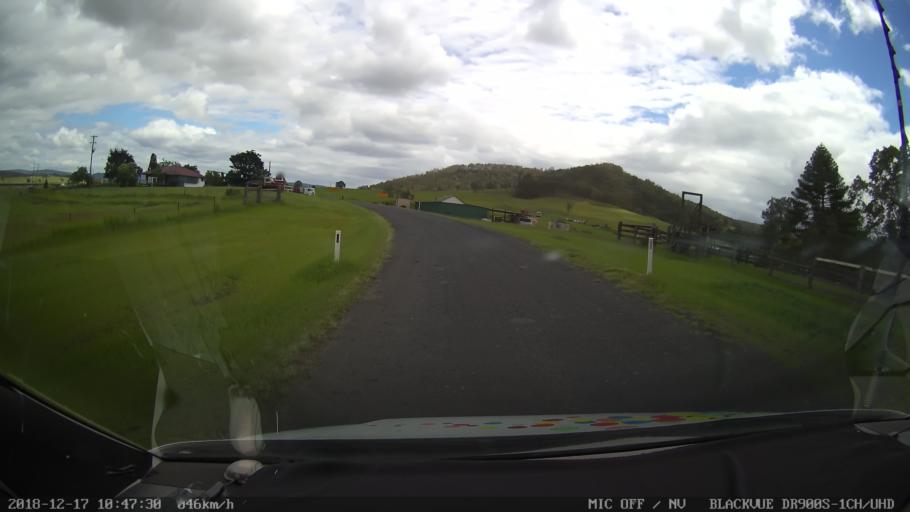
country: AU
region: New South Wales
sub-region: Clarence Valley
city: Gordon
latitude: -28.8802
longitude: 152.5711
